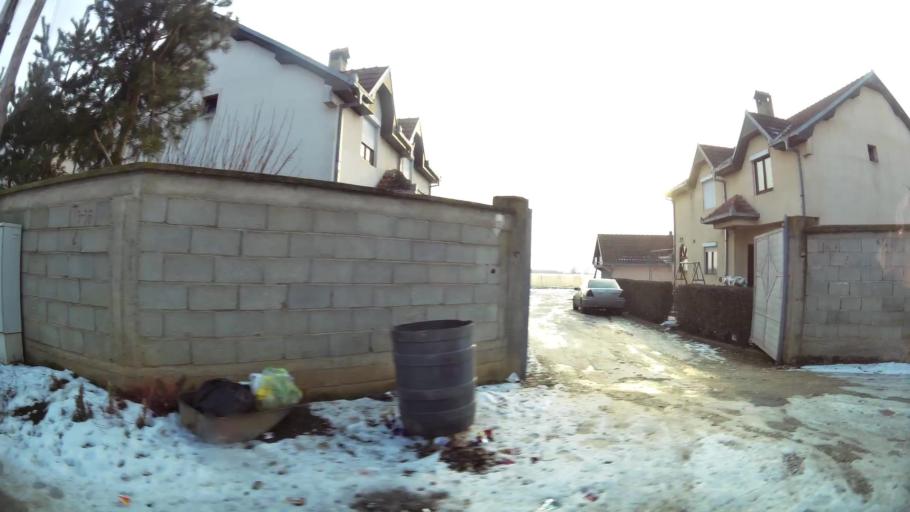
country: MK
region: Aracinovo
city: Arachinovo
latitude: 42.0198
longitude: 21.5654
